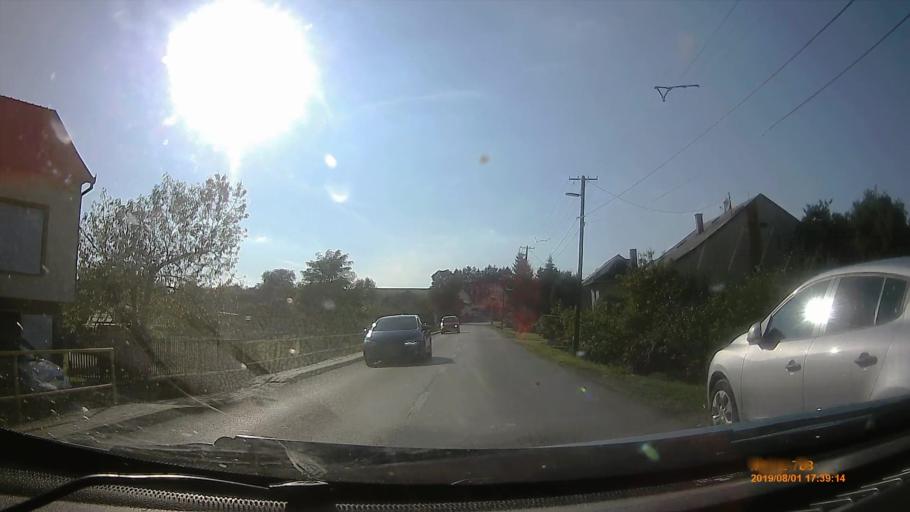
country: HU
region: Baranya
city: Komlo
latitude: 46.1966
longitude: 18.1939
